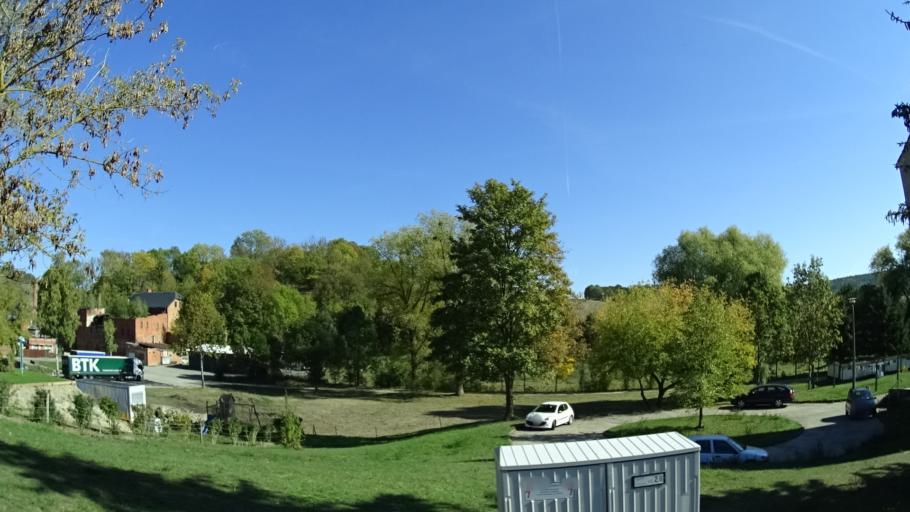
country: DE
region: Thuringia
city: Rittersdorf
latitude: 50.7631
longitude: 11.2315
